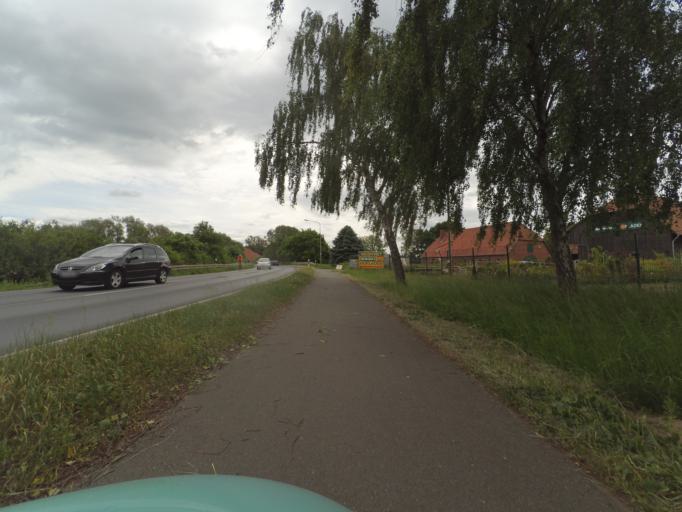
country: DE
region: Lower Saxony
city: Wunstorf
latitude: 52.4379
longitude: 9.4480
